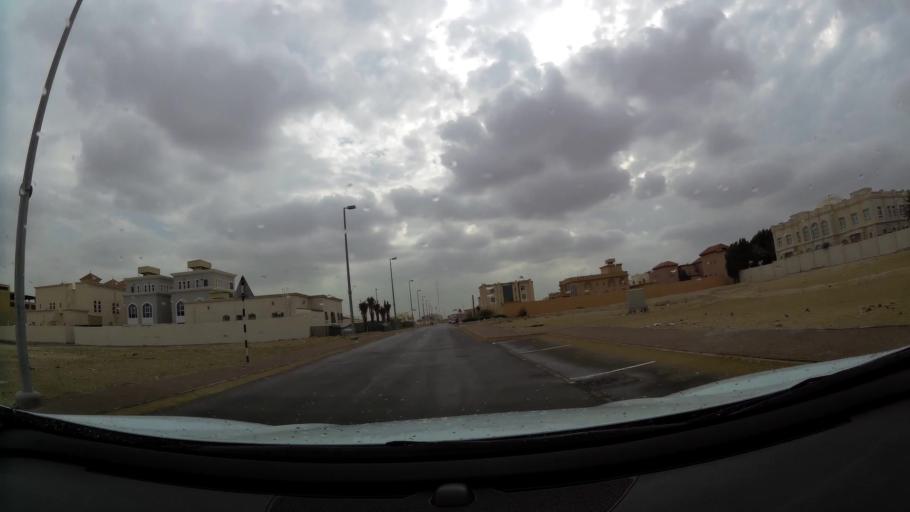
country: AE
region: Abu Dhabi
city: Abu Dhabi
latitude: 24.3582
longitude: 54.6163
